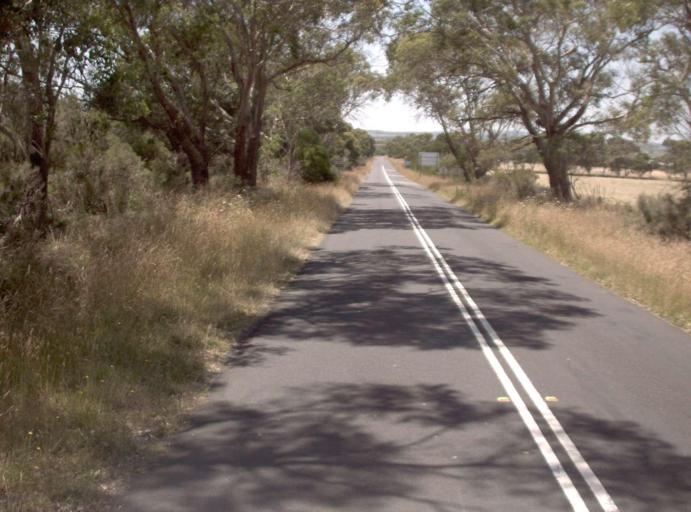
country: AU
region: Victoria
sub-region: Bass Coast
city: North Wonthaggi
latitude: -38.6621
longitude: 145.9310
